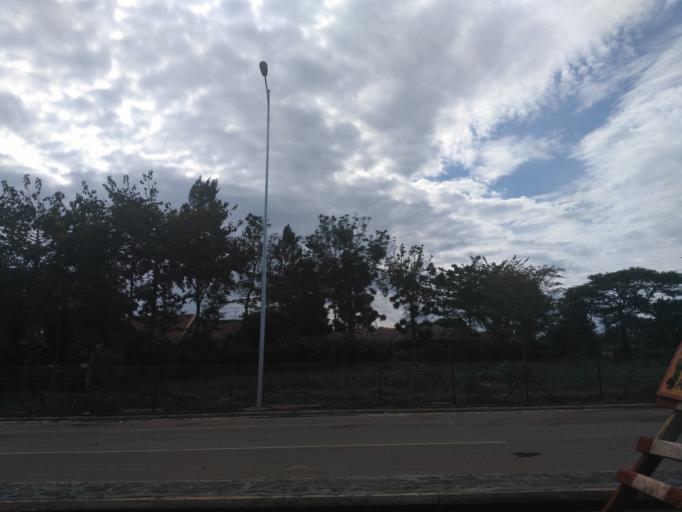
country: UG
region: Eastern Region
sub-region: Jinja District
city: Jinja
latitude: 0.4404
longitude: 33.1928
